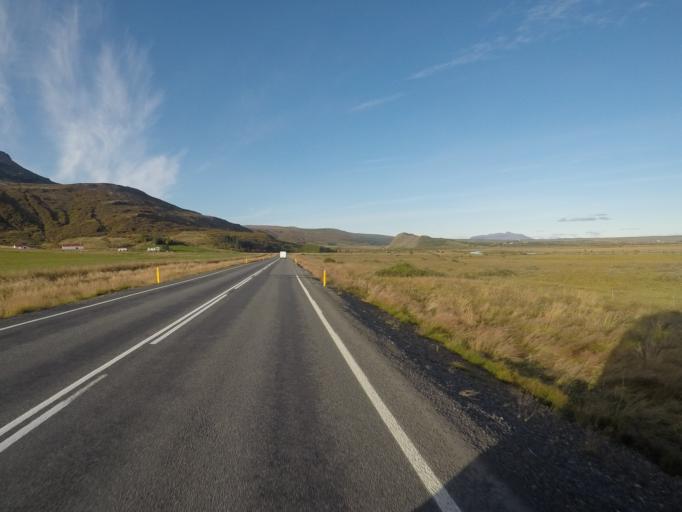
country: IS
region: South
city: Selfoss
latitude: 64.2970
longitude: -20.3331
